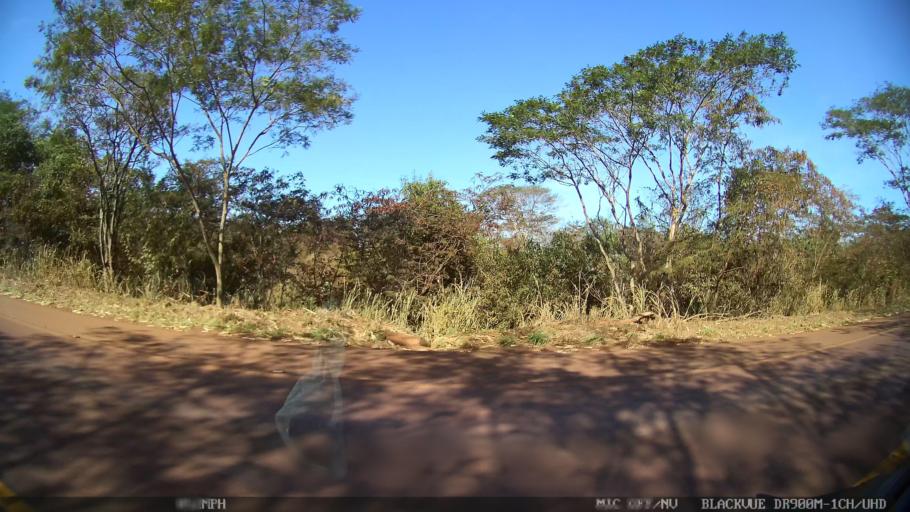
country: BR
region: Sao Paulo
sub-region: Barretos
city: Barretos
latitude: -20.4554
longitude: -48.4598
